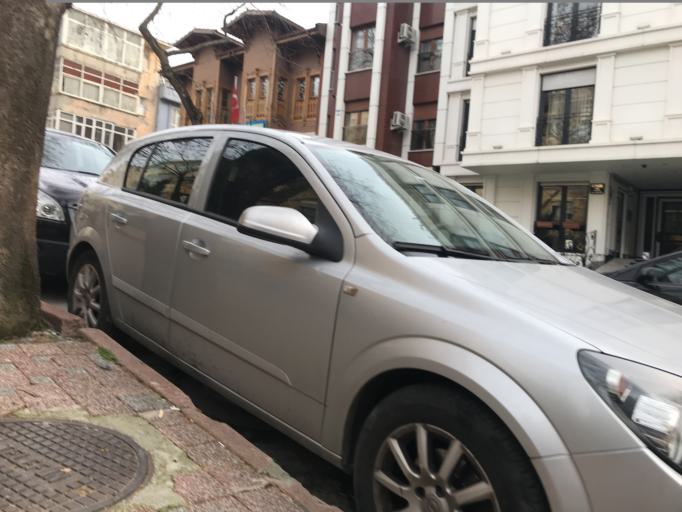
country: TR
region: Istanbul
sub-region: Atasehir
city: Atasehir
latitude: 40.9598
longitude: 29.0922
